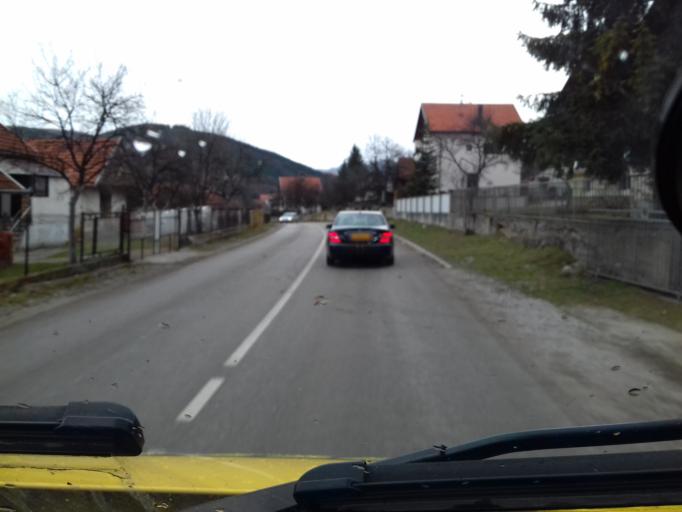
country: BA
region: Federation of Bosnia and Herzegovina
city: Turbe
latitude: 44.2472
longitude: 17.5687
